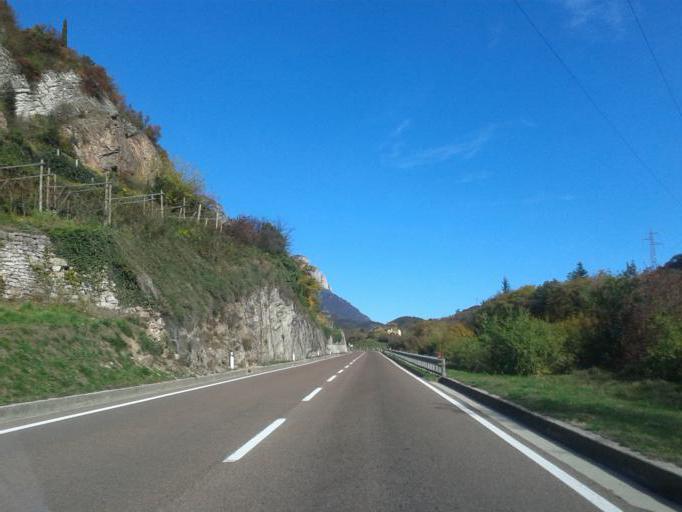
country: IT
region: Trentino-Alto Adige
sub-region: Provincia di Trento
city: Padergnone
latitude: 46.0687
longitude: 10.9915
